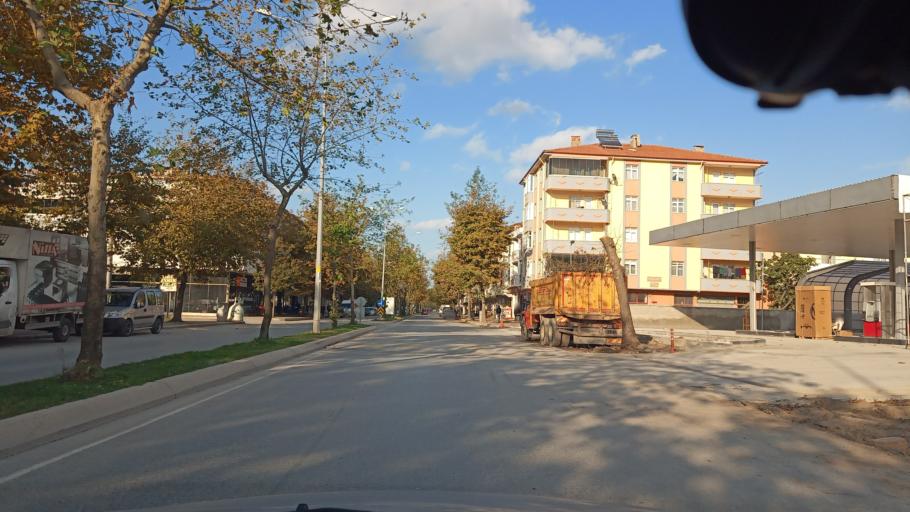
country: TR
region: Sakarya
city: Karasu
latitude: 41.0975
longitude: 30.6879
